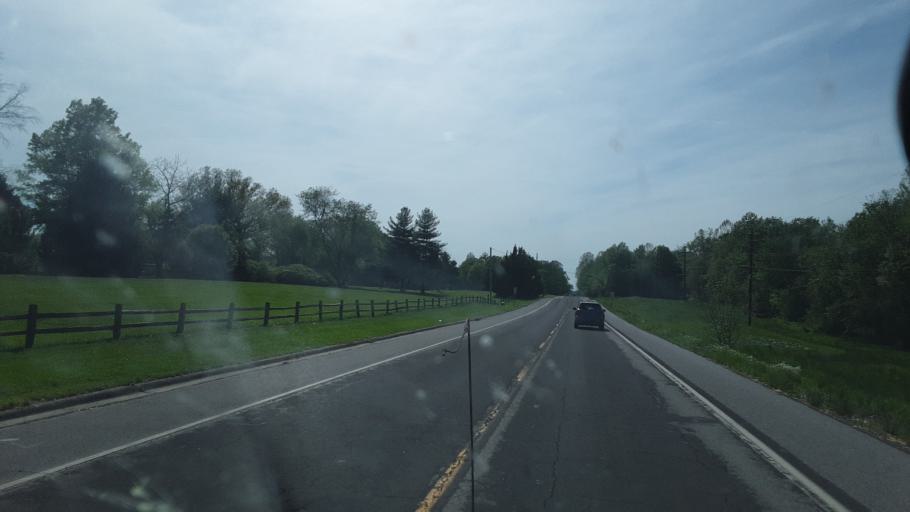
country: US
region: Illinois
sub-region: Jackson County
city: Carbondale
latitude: 37.7007
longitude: -89.2286
